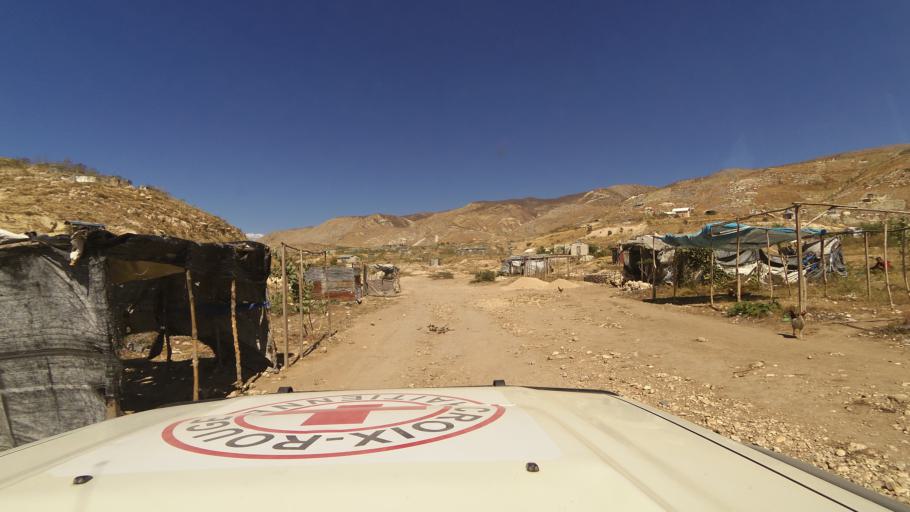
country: HT
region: Ouest
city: Croix des Bouquets
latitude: 18.6703
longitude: -72.2847
